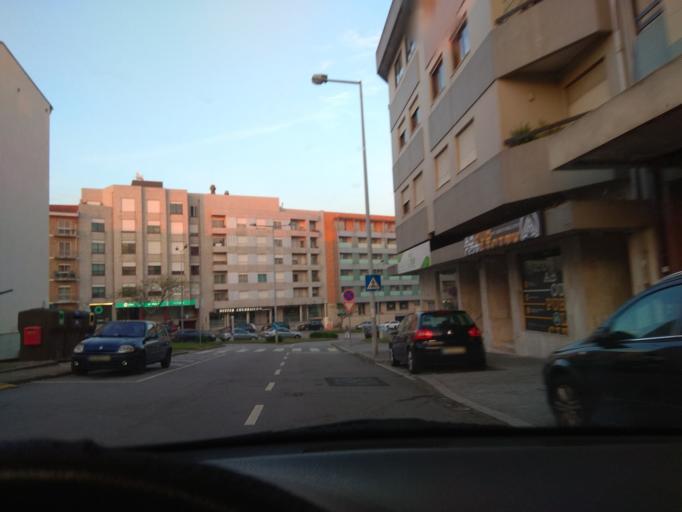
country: PT
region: Porto
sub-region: Maia
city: Maia
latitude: 41.2285
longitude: -8.6207
